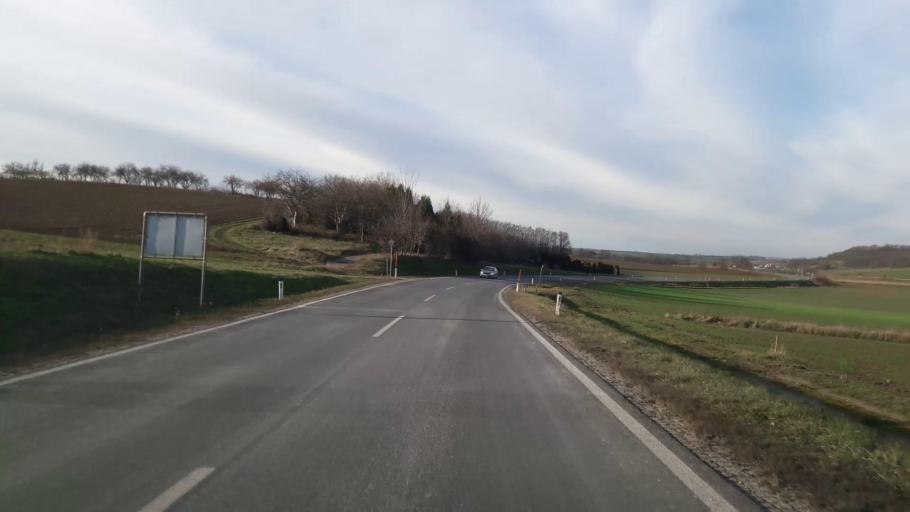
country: AT
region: Lower Austria
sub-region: Politischer Bezirk Ganserndorf
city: Gross-Schweinbarth
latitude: 48.4215
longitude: 16.6279
